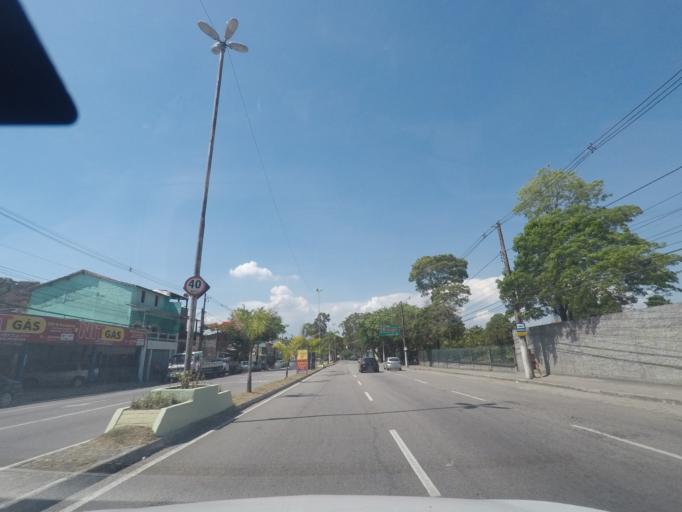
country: BR
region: Rio de Janeiro
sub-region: Niteroi
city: Niteroi
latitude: -22.9138
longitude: -43.0479
